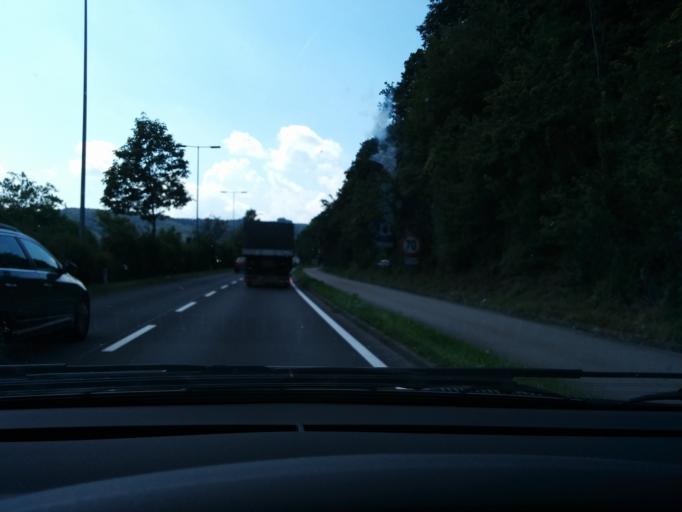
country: AT
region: Upper Austria
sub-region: Politischer Bezirk Linz-Land
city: Leonding
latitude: 48.3120
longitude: 14.2402
